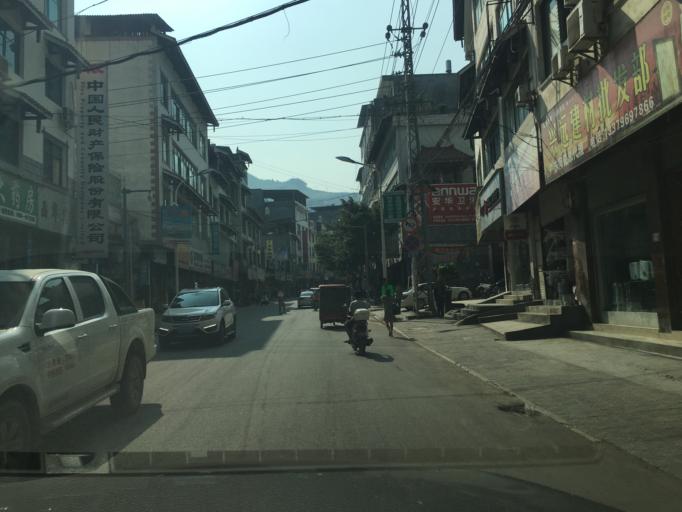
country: CN
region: Guangxi Zhuangzu Zizhiqu
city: Xinzhou
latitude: 24.9872
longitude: 105.8034
